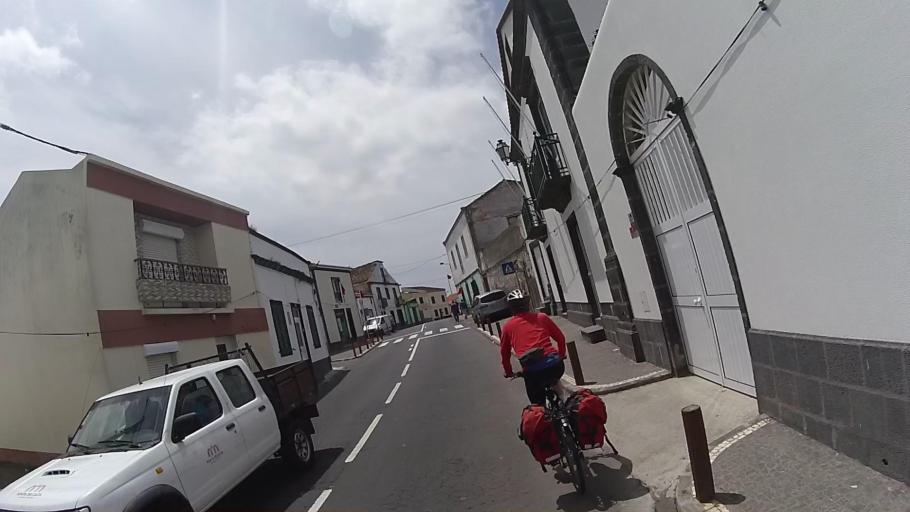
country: PT
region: Azores
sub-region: Ponta Delgada
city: Rosto de Cao
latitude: 37.7494
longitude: -25.6330
